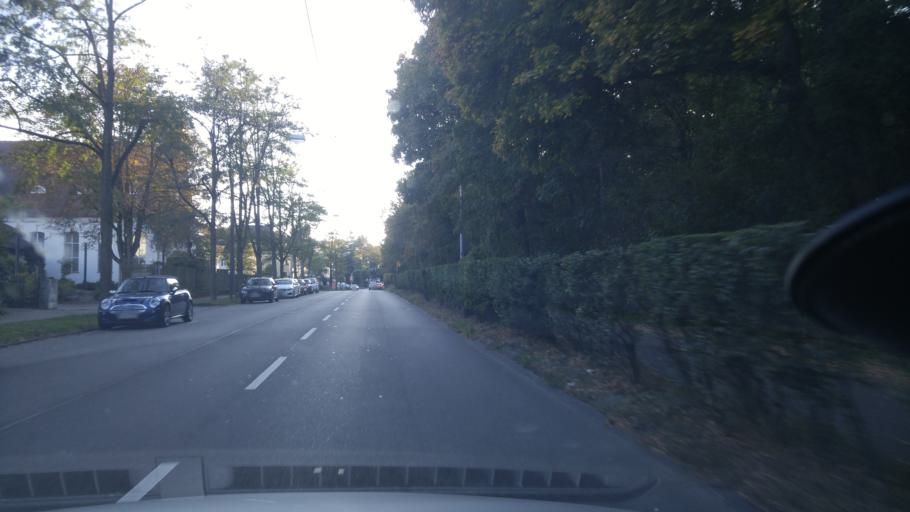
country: DE
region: Baden-Wuerttemberg
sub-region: Regierungsbezirk Stuttgart
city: Stuttgart Feuerbach
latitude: 48.7854
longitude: 9.1486
